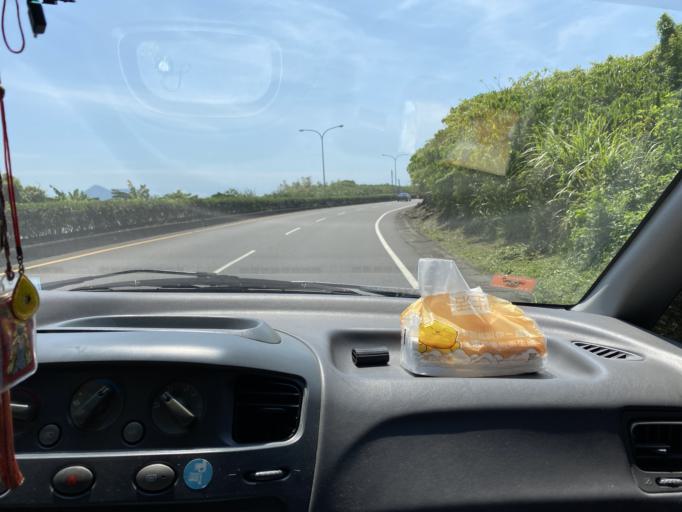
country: TW
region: Taiwan
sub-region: Yilan
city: Yilan
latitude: 24.9280
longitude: 121.8859
